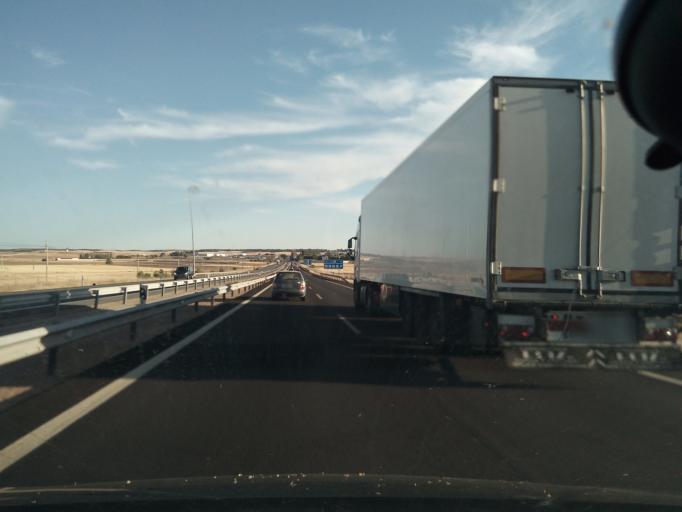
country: ES
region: Castille-La Mancha
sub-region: Province of Toledo
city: Tembleque
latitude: 39.7094
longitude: -3.4965
